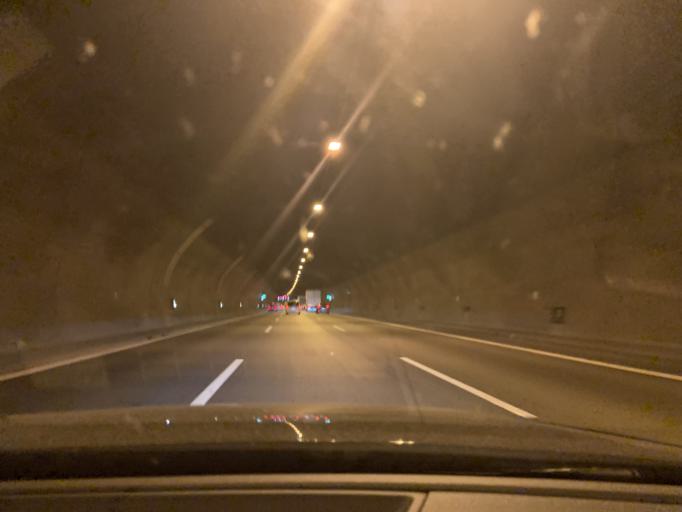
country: DE
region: Baden-Wuerttemberg
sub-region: Regierungsbezirk Stuttgart
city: Leonberg
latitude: 48.7935
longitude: 9.0241
